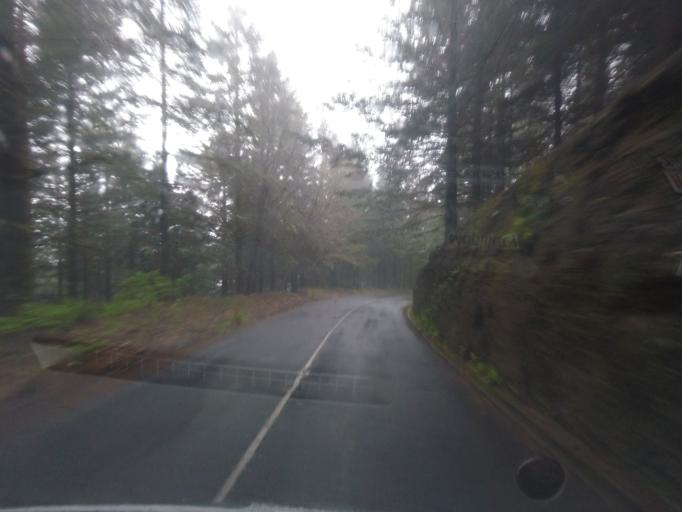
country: PT
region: Madeira
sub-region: Funchal
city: Nossa Senhora do Monte
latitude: 32.7153
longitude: -16.8863
